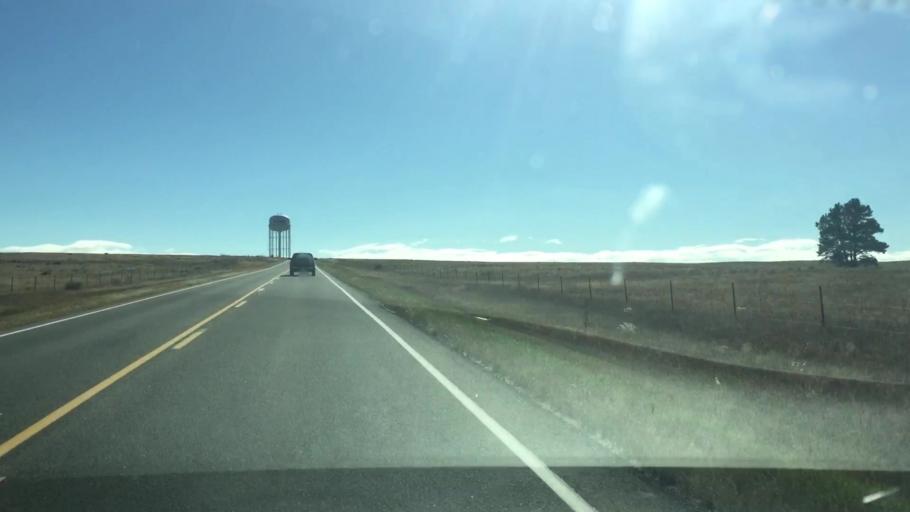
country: US
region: Colorado
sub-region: Elbert County
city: Kiowa
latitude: 39.3419
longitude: -104.4429
